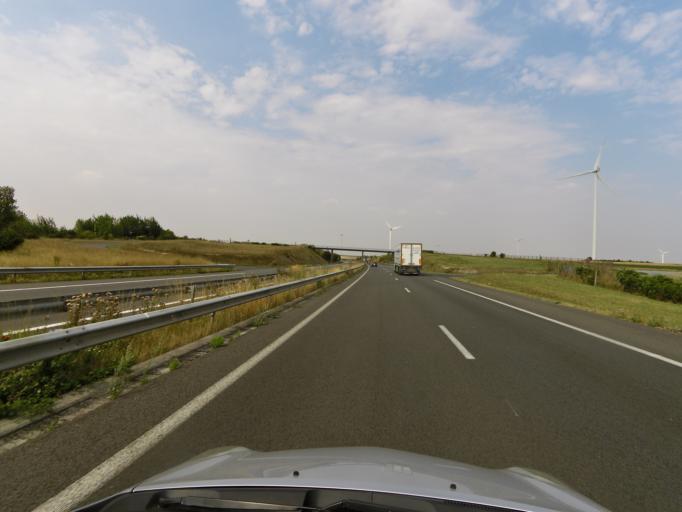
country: FR
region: Picardie
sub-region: Departement de l'Aisne
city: Holnon
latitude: 49.8878
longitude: 3.2549
